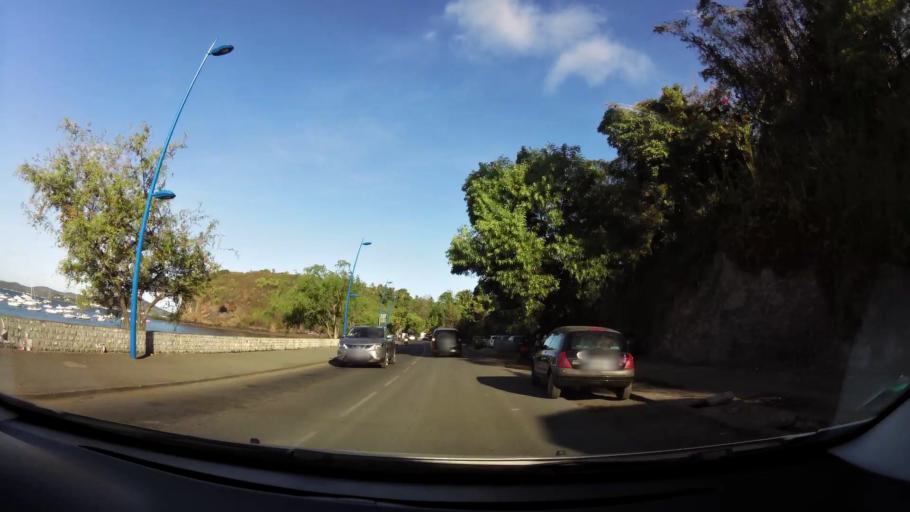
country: YT
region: Mamoudzou
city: Mamoudzou
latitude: -12.7800
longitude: 45.2329
